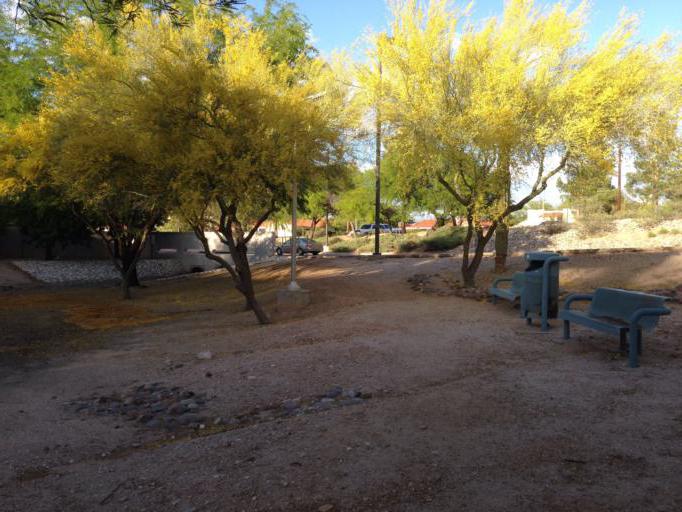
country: US
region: Arizona
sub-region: Pima County
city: Tucson
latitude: 32.2389
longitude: -110.9448
